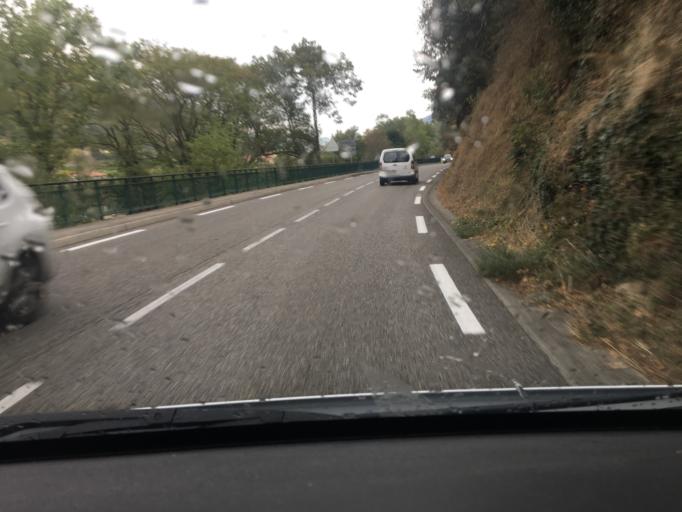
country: FR
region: Rhone-Alpes
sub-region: Departement de l'Ardeche
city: Saint-Jean-de-Muzols
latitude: 45.0662
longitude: 4.7820
